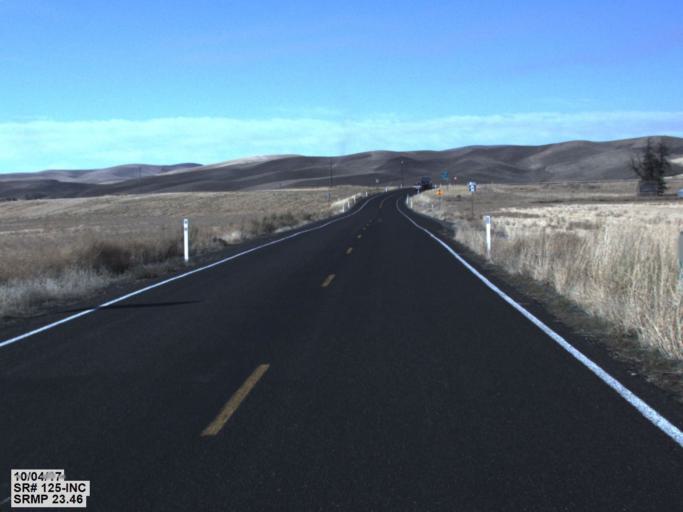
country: US
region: Washington
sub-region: Walla Walla County
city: Waitsburg
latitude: 46.2957
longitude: -118.3405
